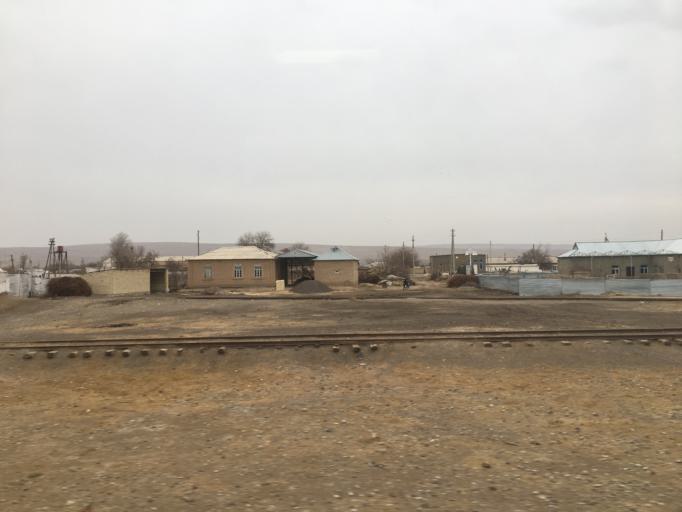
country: TM
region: Mary
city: Yoloeten
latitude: 36.5417
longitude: 62.5536
